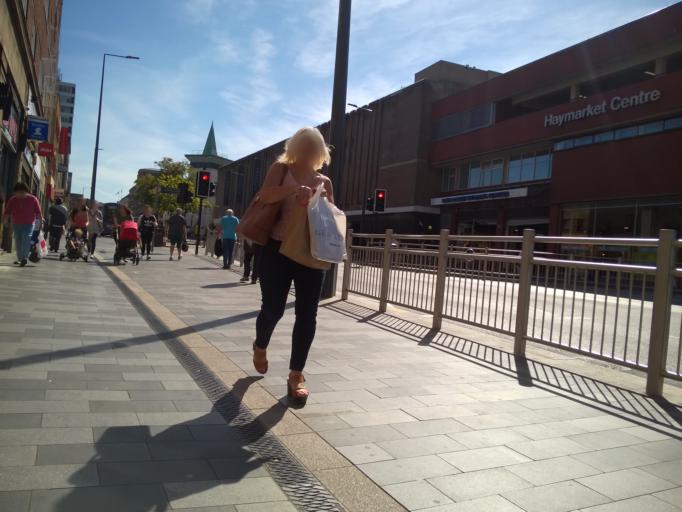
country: GB
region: England
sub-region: City of Leicester
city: Leicester
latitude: 52.6373
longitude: -1.1305
